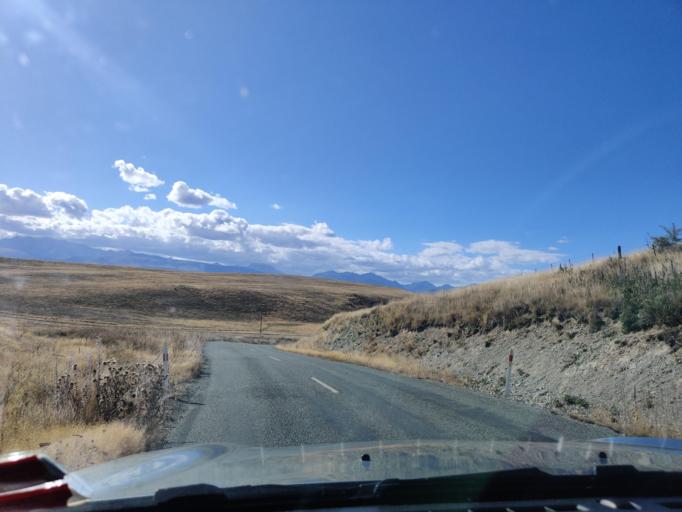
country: NZ
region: Canterbury
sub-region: Timaru District
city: Pleasant Point
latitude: -43.9754
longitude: 170.4642
